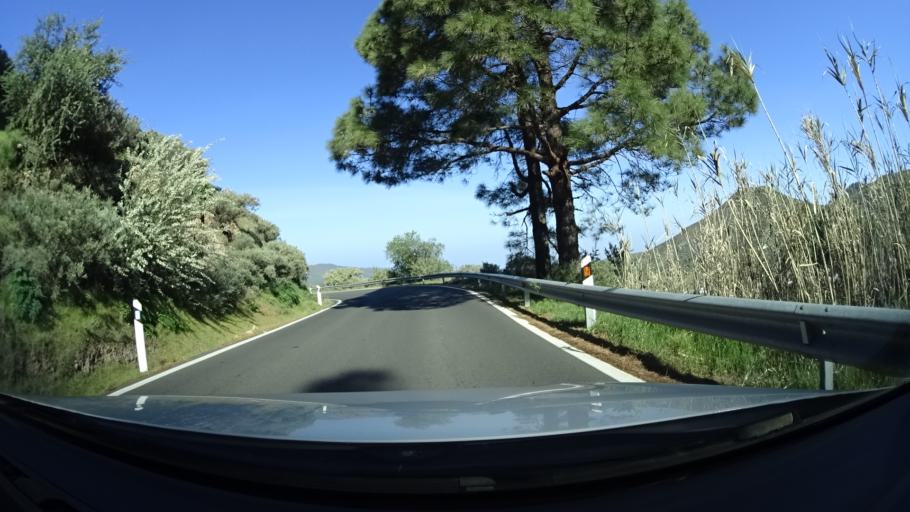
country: ES
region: Canary Islands
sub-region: Provincia de Las Palmas
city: Artenara
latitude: 28.0256
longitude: -15.6322
